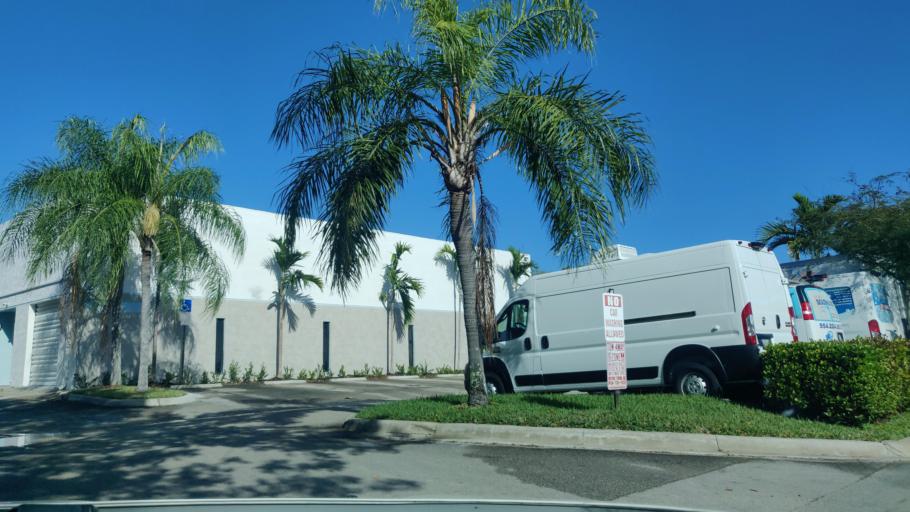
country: US
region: Florida
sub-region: Broward County
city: Tamarac
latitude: 26.1846
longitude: -80.2876
